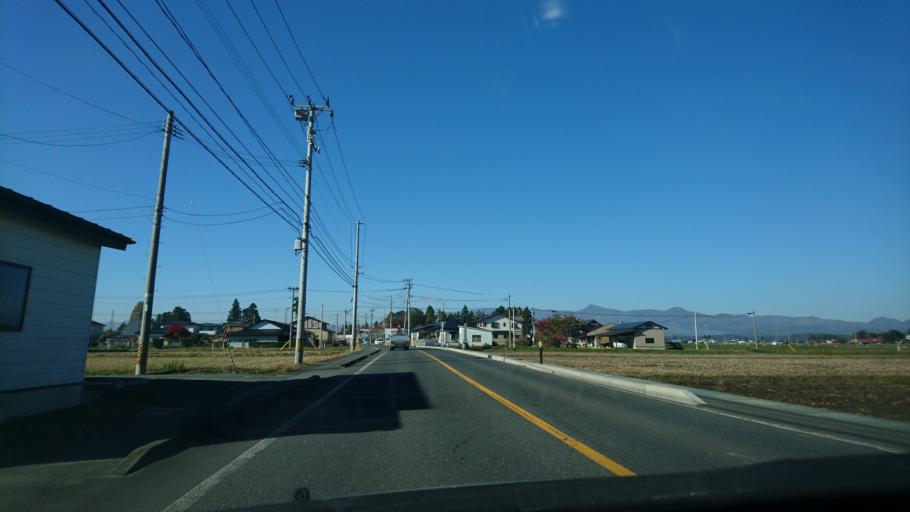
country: JP
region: Iwate
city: Mizusawa
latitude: 39.1421
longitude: 141.0967
